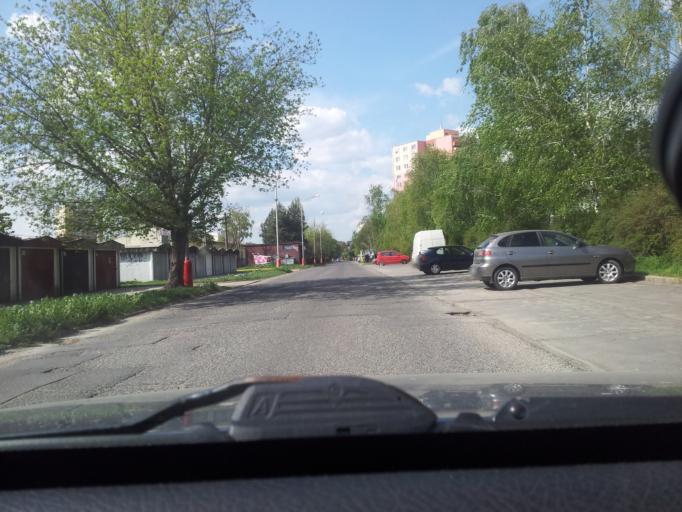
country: SK
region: Nitriansky
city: Levice
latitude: 48.2075
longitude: 18.6013
